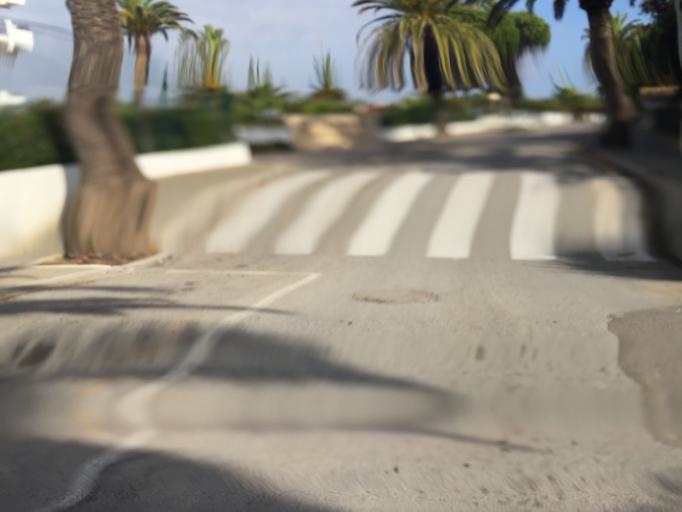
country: ES
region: Andalusia
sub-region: Provincia de Cadiz
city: Conil de la Frontera
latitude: 36.2922
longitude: -6.1100
